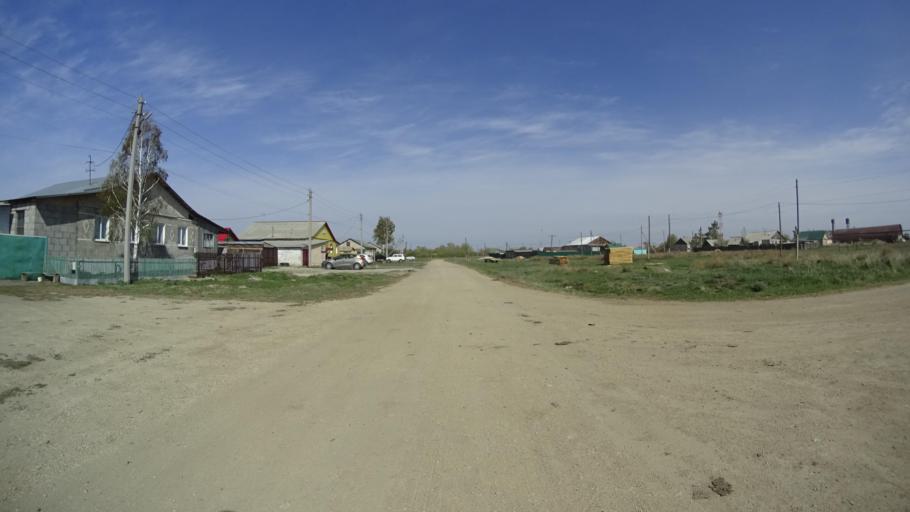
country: RU
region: Chelyabinsk
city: Chesma
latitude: 53.7885
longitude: 61.0388
